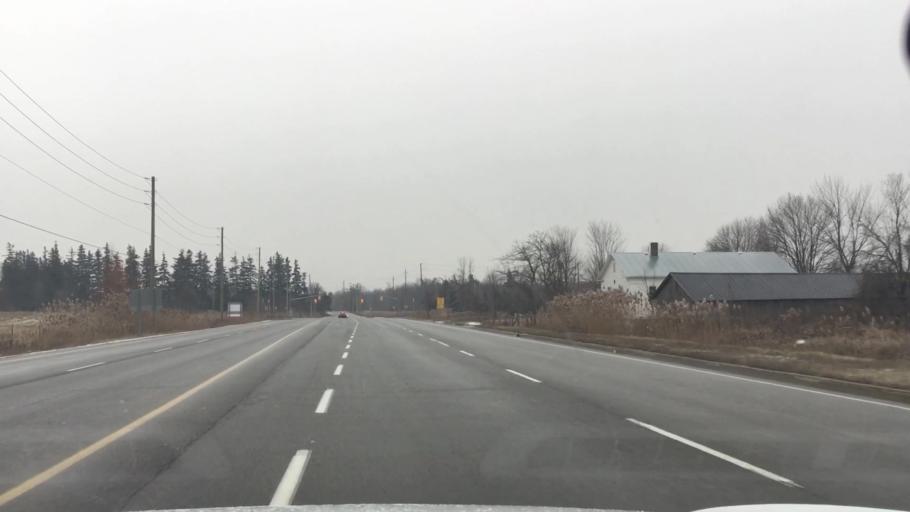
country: CA
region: Ontario
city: Pickering
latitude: 43.8579
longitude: -79.1711
